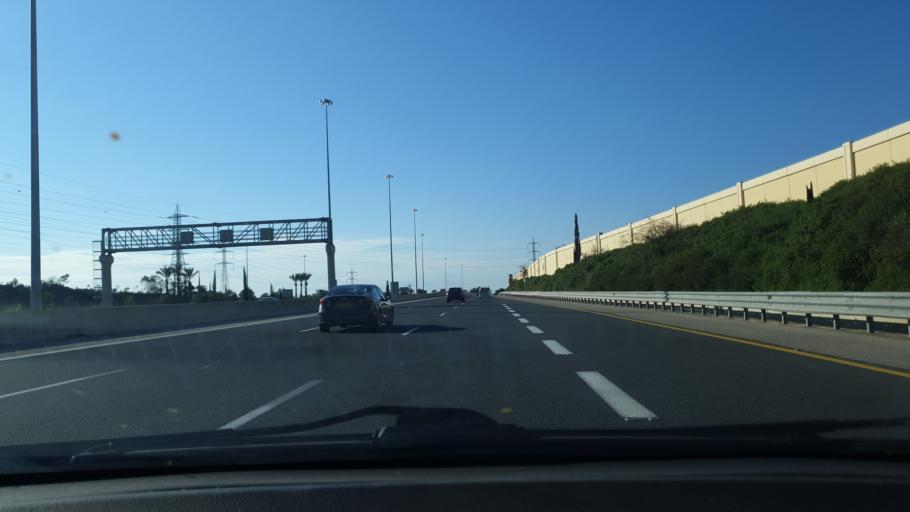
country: IL
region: Central District
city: Rishon LeZiyyon
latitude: 31.9660
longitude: 34.7632
